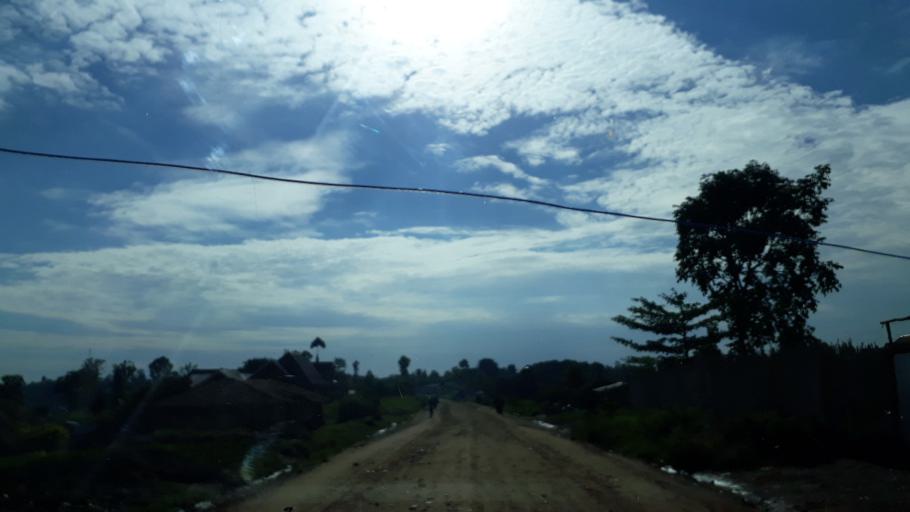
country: UG
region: Northern Region
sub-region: Zombo District
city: Paidha
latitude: 2.2982
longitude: 31.0053
